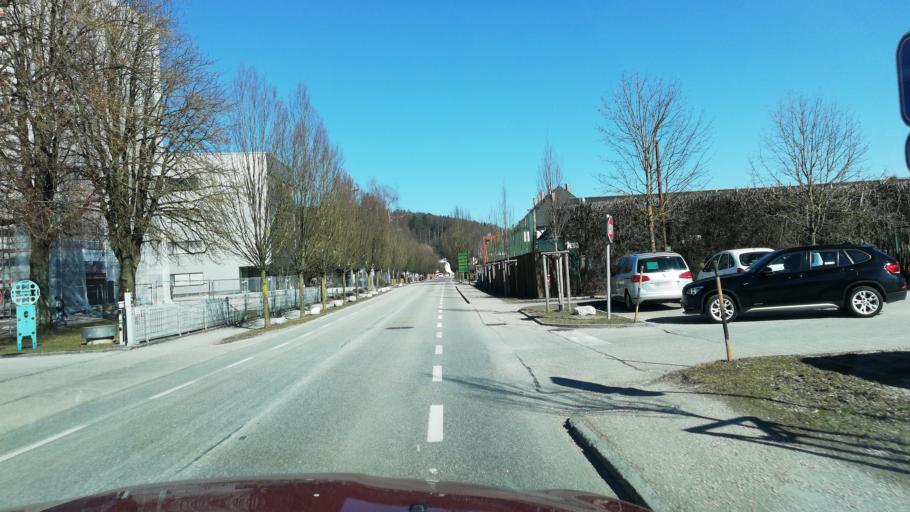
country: AT
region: Upper Austria
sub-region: Politischer Bezirk Vocklabruck
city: Attnang-Puchheim
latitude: 48.0137
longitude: 13.7184
